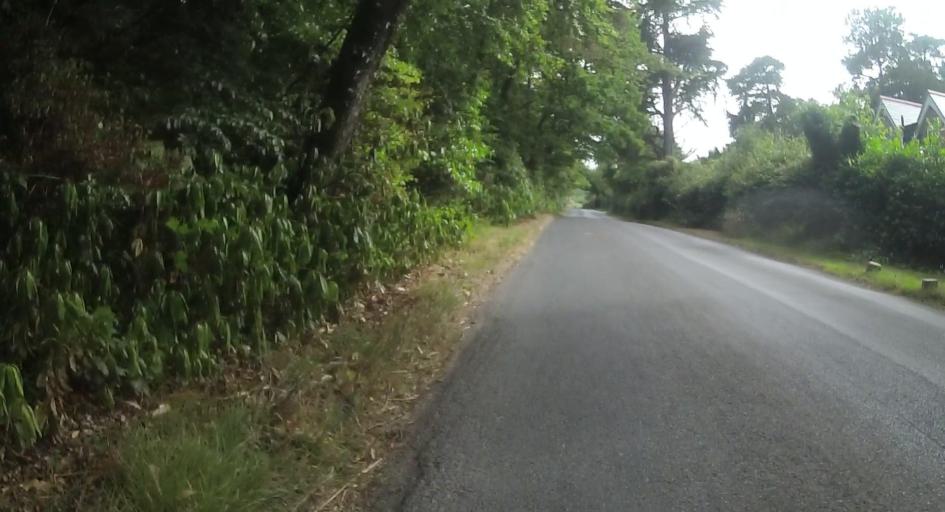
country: GB
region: England
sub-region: Dorset
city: Wareham
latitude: 50.6524
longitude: -2.1179
